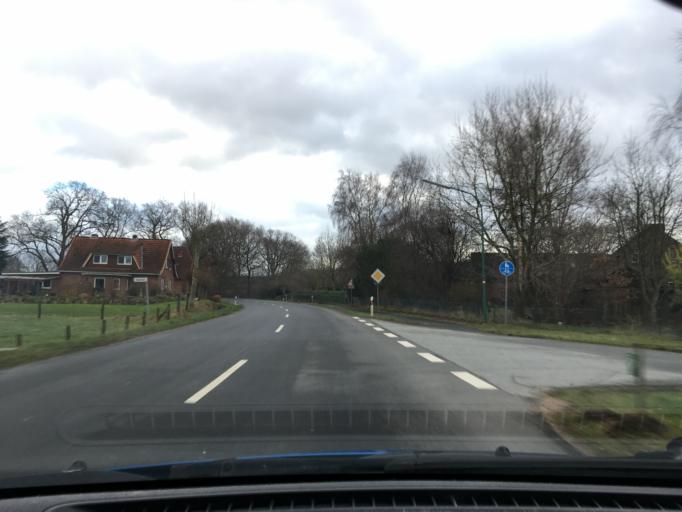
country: DE
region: Schleswig-Holstein
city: Kaaks
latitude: 53.9876
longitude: 9.4794
